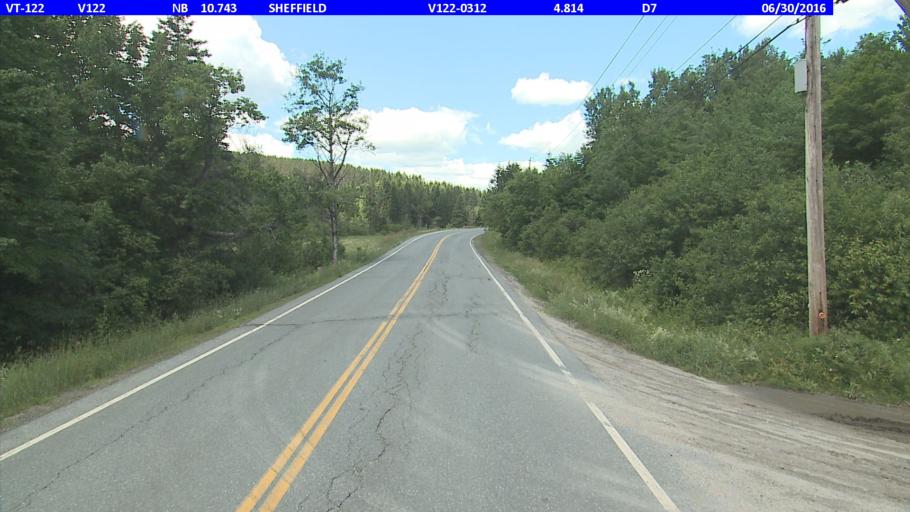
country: US
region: Vermont
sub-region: Caledonia County
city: Lyndonville
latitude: 44.6399
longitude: -72.1522
